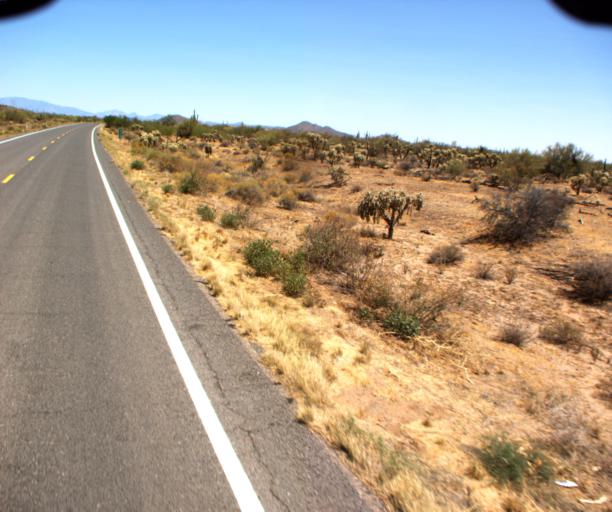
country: US
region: Arizona
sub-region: Pinal County
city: Florence
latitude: 32.7933
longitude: -111.1760
